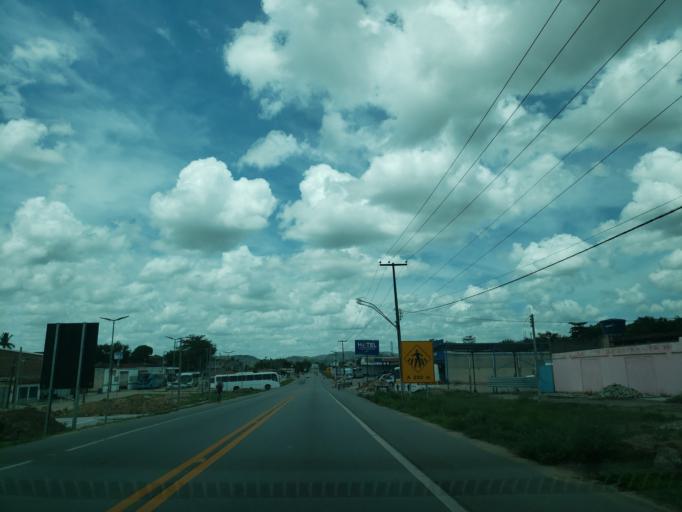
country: BR
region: Alagoas
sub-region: Uniao Dos Palmares
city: Uniao dos Palmares
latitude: -9.1638
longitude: -36.0188
